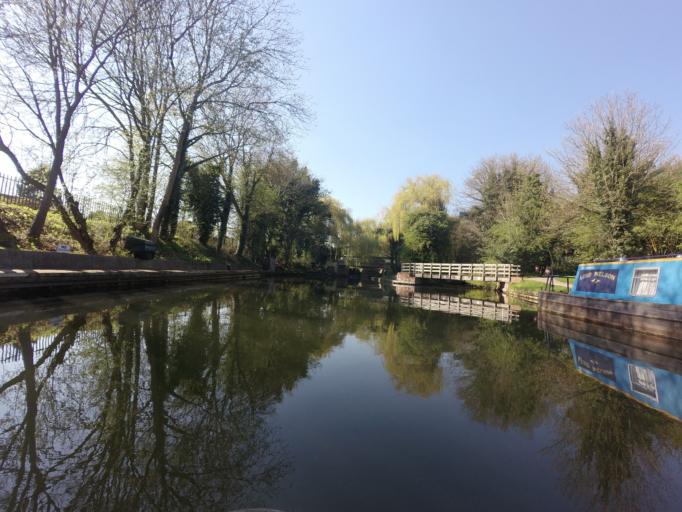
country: GB
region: England
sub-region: Hertfordshire
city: Kings Langley
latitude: 51.7272
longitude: -0.4518
